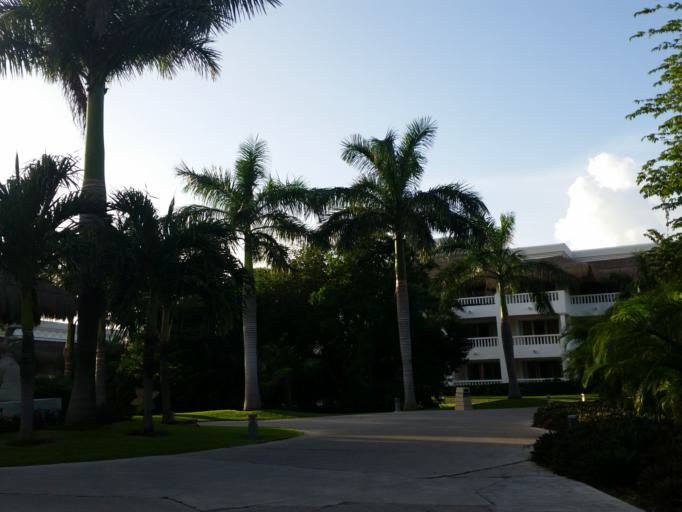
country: MX
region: Quintana Roo
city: Playa del Carmen
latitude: 20.6696
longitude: -87.0285
